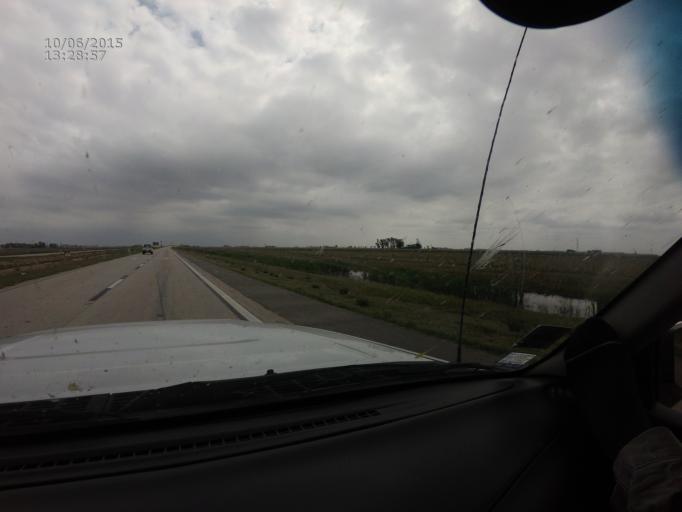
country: AR
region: Cordoba
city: Leones
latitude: -32.6402
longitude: -62.2342
